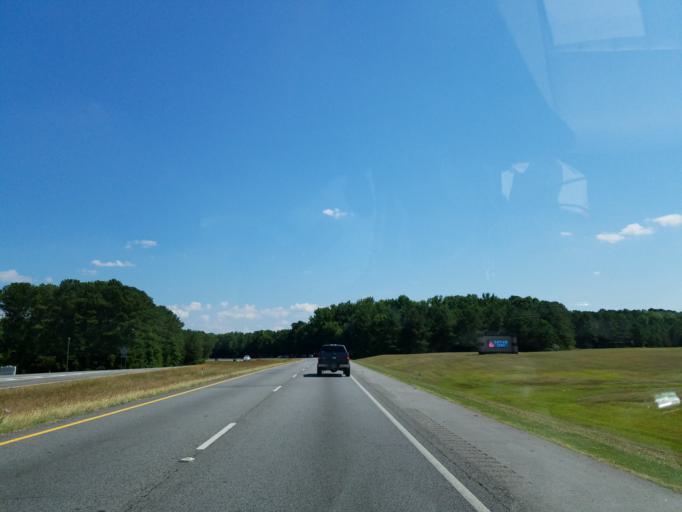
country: US
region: Georgia
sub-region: Spalding County
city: Griffin
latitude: 33.2063
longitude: -84.2890
